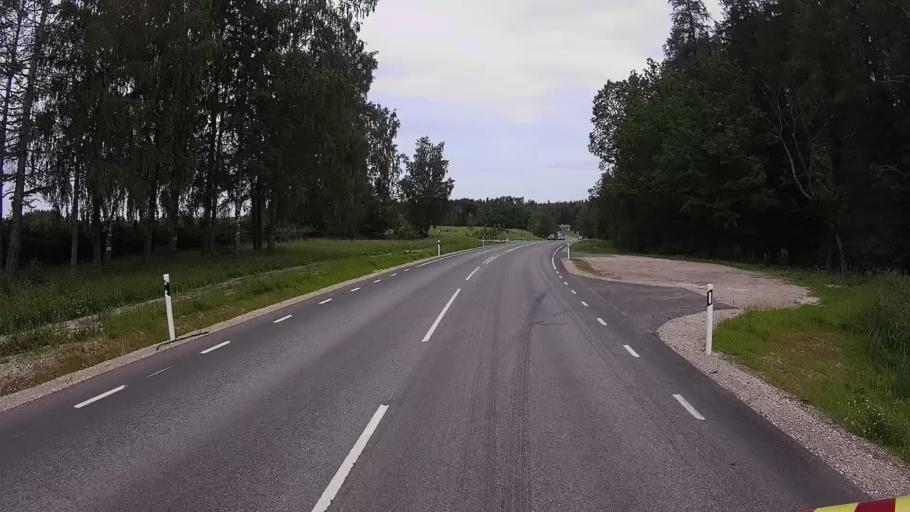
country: EE
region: Viljandimaa
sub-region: Viljandi linn
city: Viljandi
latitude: 58.2783
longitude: 25.5826
